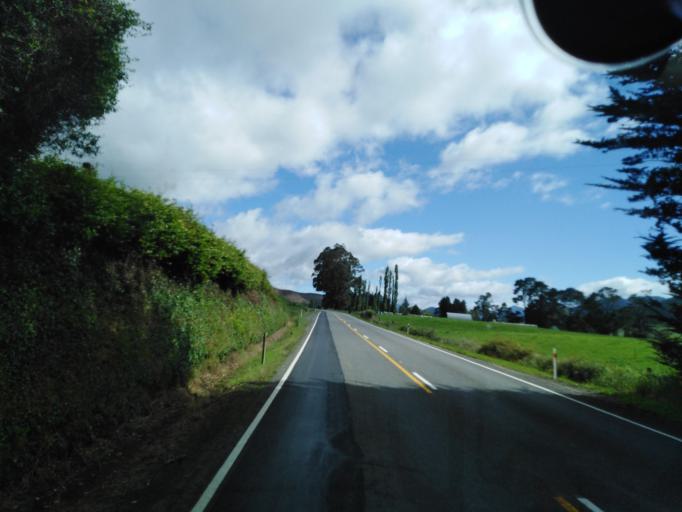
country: NZ
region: Nelson
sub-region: Nelson City
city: Nelson
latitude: -41.2791
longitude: 173.5735
